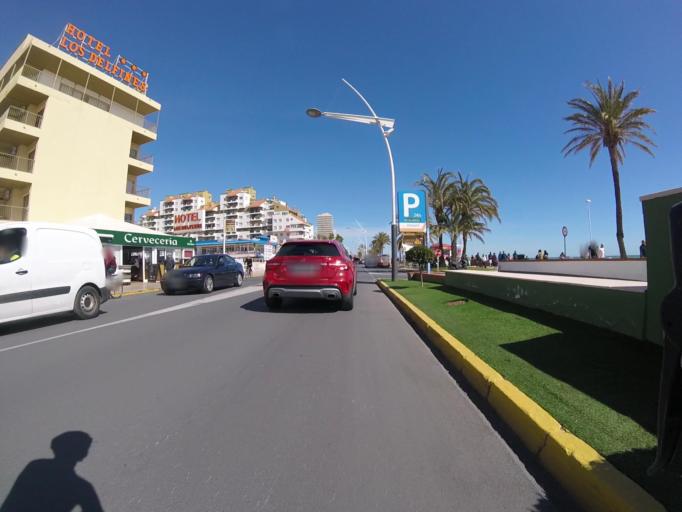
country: ES
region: Valencia
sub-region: Provincia de Castello
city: Peniscola
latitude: 40.3623
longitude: 0.4025
